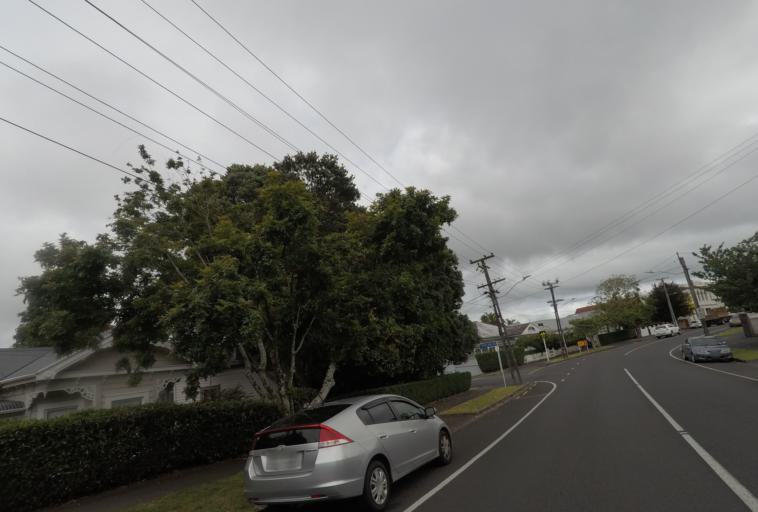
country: NZ
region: Auckland
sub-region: Auckland
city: Auckland
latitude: -36.8787
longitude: 174.7572
